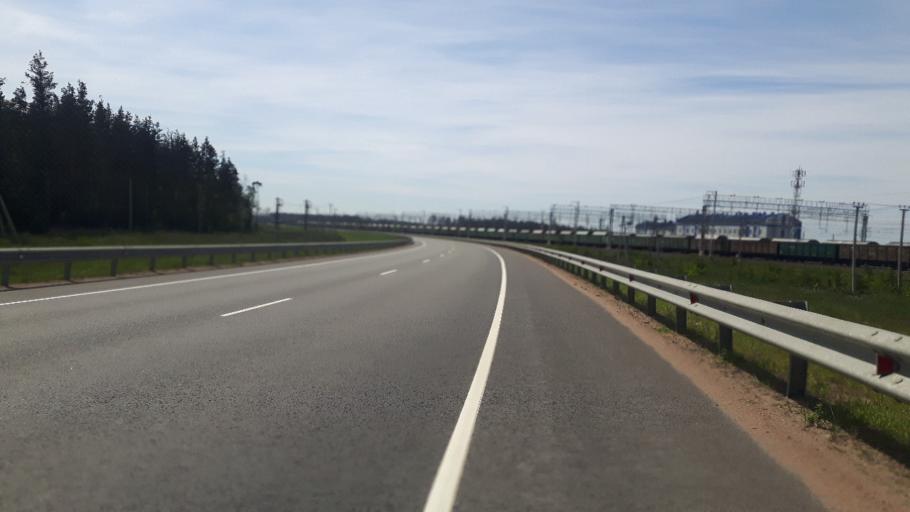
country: RU
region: Leningrad
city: Vistino
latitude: 59.6728
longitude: 28.4340
